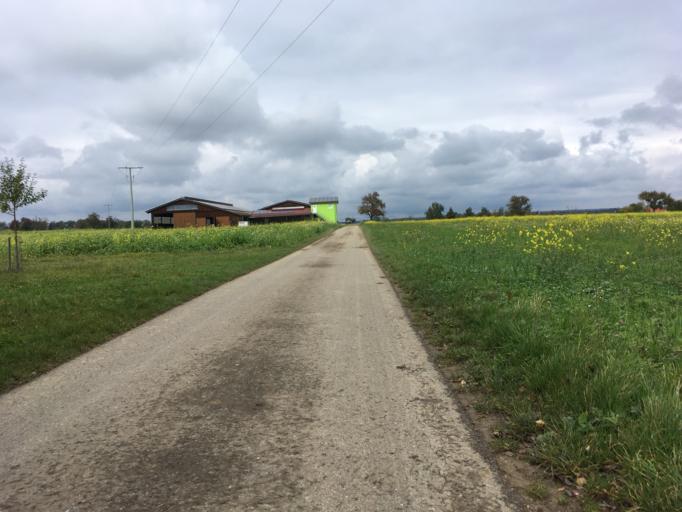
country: DE
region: Baden-Wuerttemberg
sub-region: Tuebingen Region
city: Gomaringen
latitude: 48.4926
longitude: 9.0939
